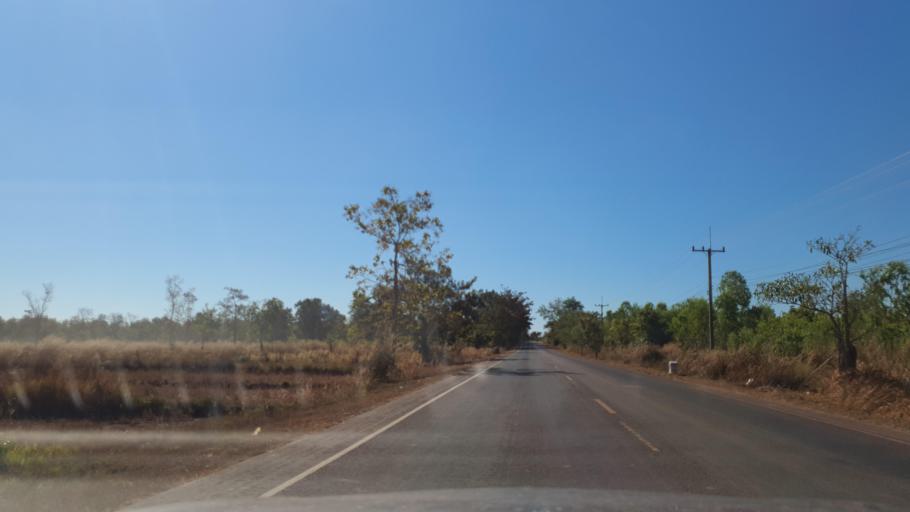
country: TH
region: Nakhon Phanom
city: Si Songkhram
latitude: 17.7407
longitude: 104.2861
